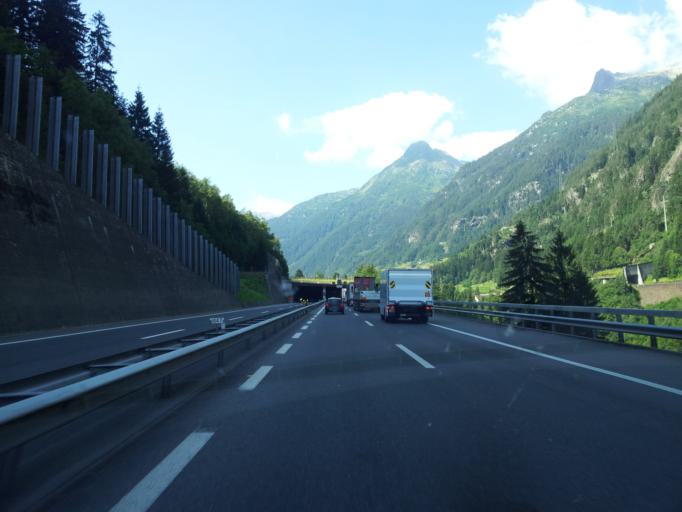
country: CH
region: Uri
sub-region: Uri
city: Andermatt
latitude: 46.7192
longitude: 8.6166
